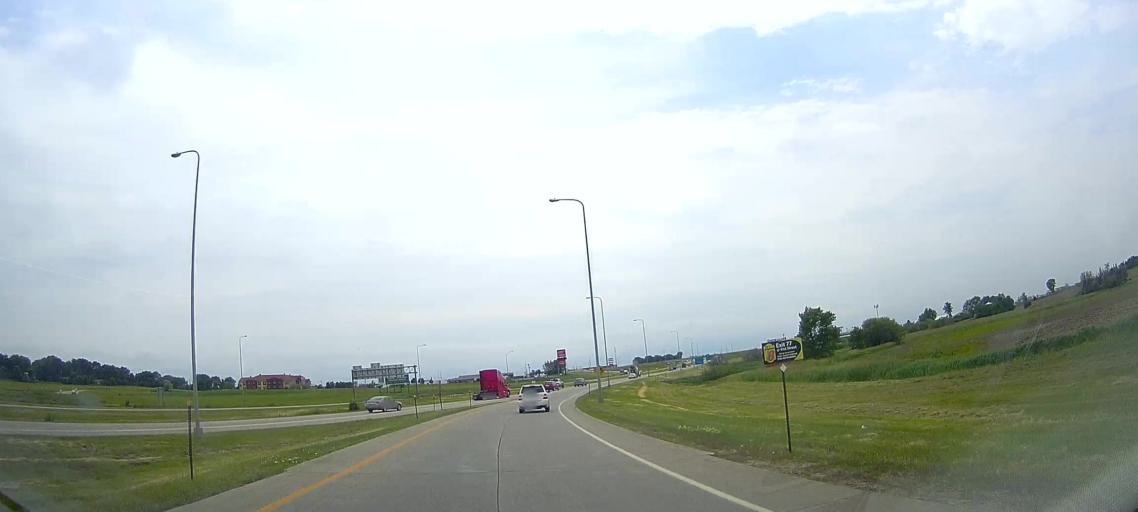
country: US
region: South Dakota
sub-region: Minnehaha County
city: Crooks
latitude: 43.6099
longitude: -96.7712
